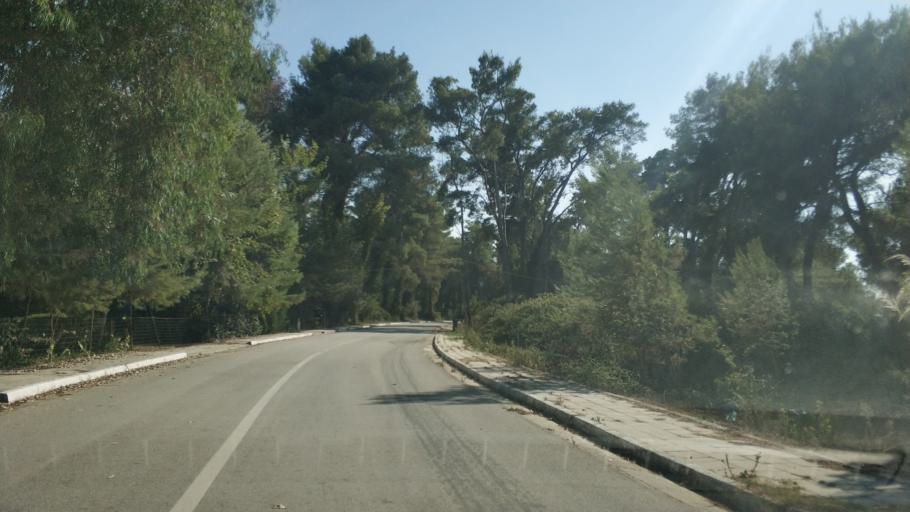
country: AL
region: Fier
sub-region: Rrethi i Lushnjes
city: Divjake
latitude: 40.9663
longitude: 19.4782
